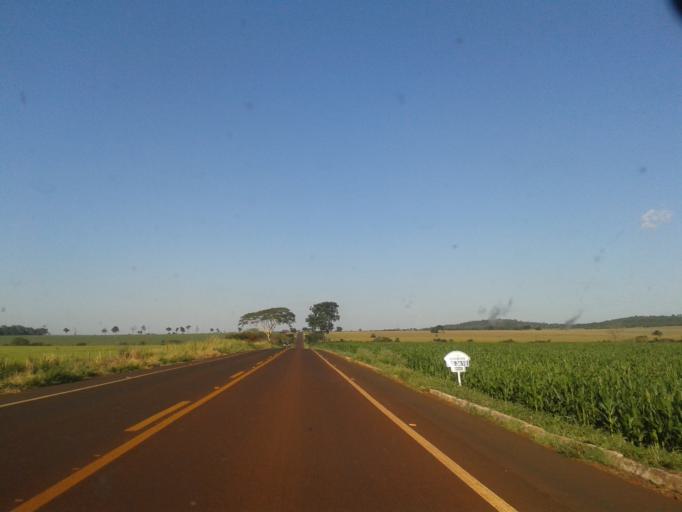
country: BR
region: Minas Gerais
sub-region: Capinopolis
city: Capinopolis
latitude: -18.7121
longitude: -49.8220
